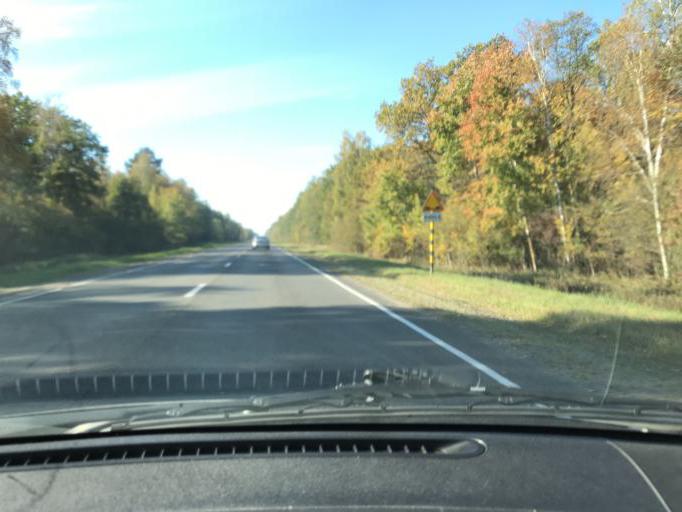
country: BY
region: Brest
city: Asnyezhytsy
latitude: 52.2615
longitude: 26.3151
